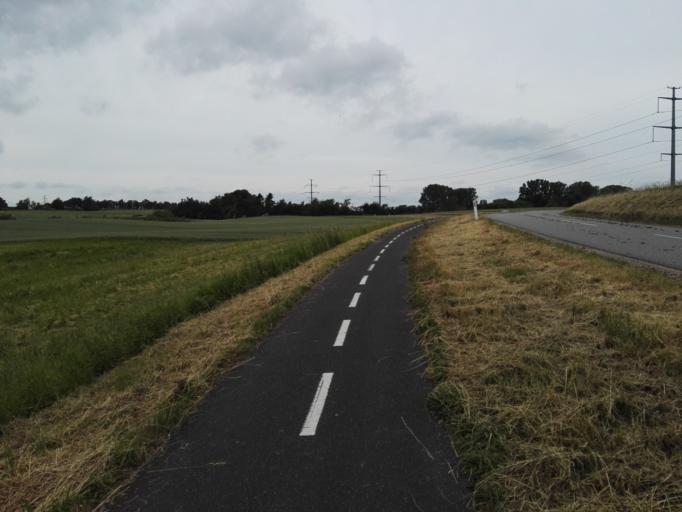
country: DK
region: Capital Region
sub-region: Egedal Kommune
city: Vekso
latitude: 55.7307
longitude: 12.2465
